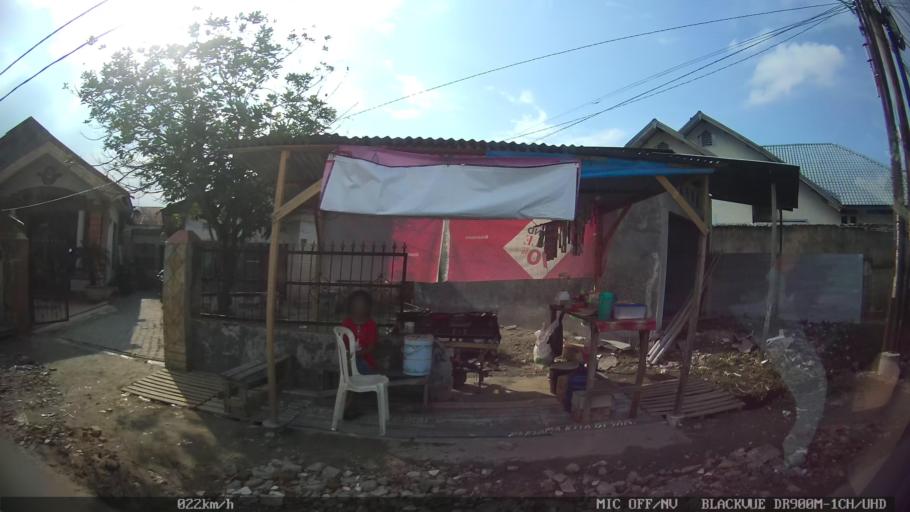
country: ID
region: North Sumatra
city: Medan
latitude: 3.5997
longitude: 98.7408
